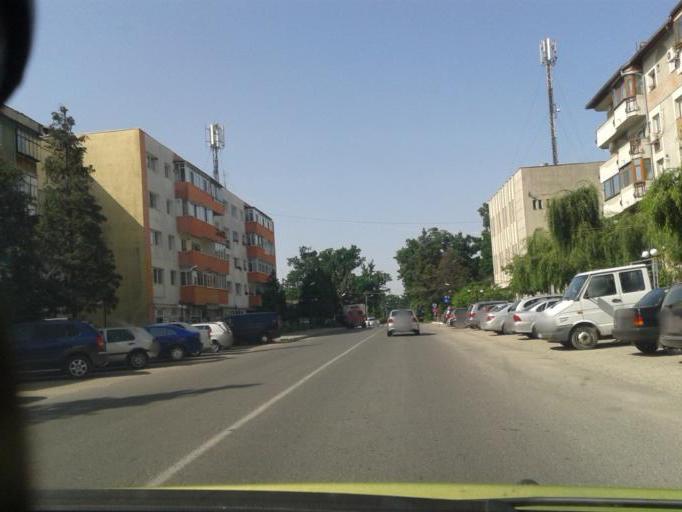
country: RO
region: Prahova
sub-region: Comuna Paulesti
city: Gageni
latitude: 45.0507
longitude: 25.9532
